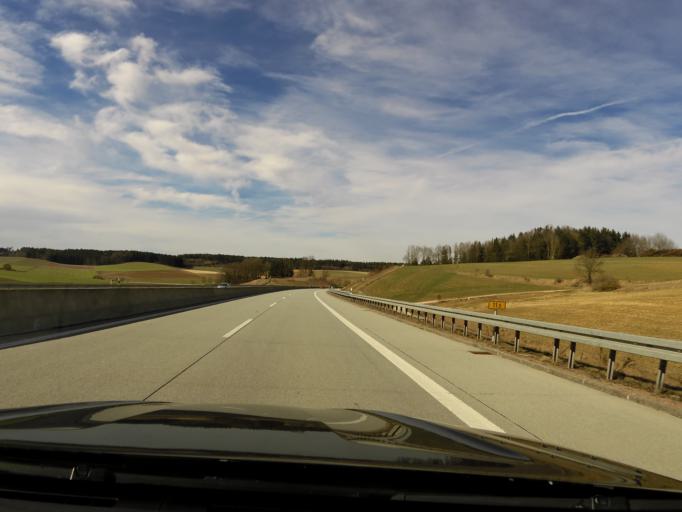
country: DE
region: Bavaria
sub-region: Upper Palatinate
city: Schierling
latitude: 48.8024
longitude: 12.1402
